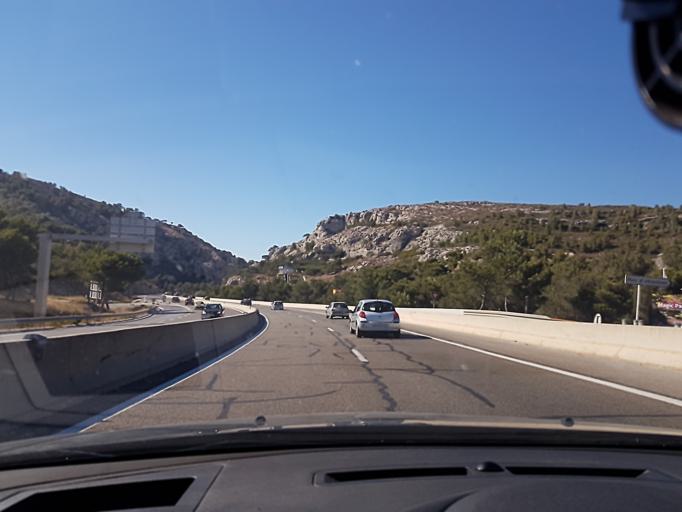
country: FR
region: Provence-Alpes-Cote d'Azur
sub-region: Departement des Bouches-du-Rhone
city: Ensues-la-Redonne
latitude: 43.3642
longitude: 5.1871
